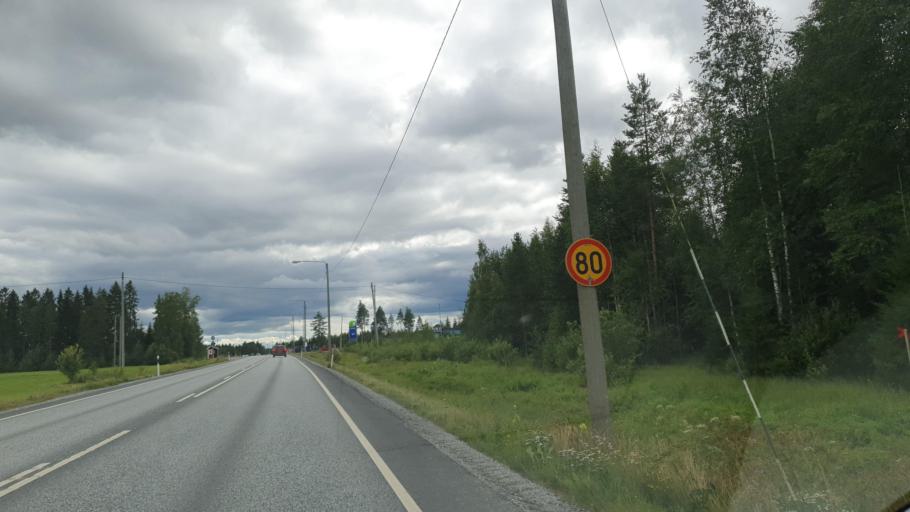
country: FI
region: Northern Savo
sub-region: Ylae-Savo
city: Sonkajaervi
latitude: 63.8710
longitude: 27.4401
